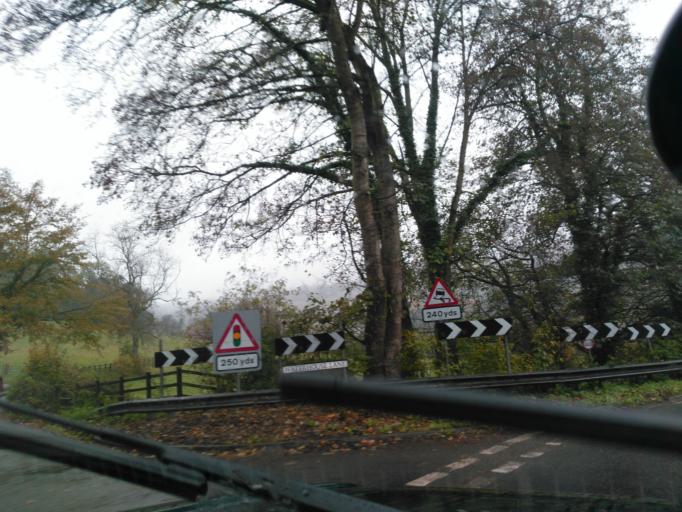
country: GB
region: England
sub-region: Bath and North East Somerset
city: Freshford
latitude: 51.3554
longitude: -2.3169
